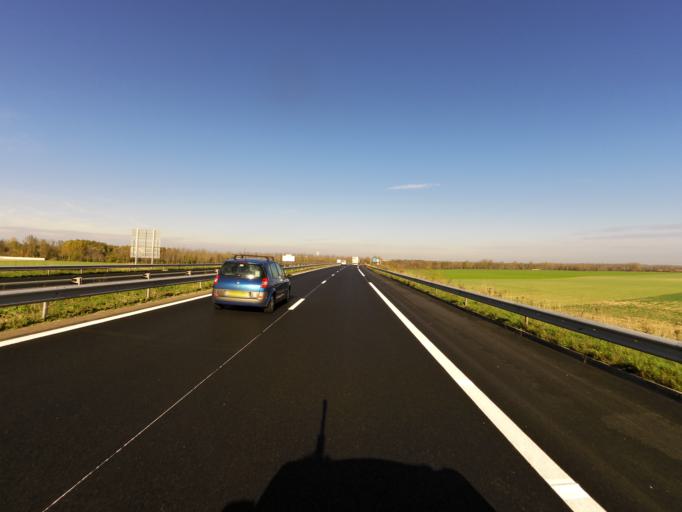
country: FR
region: Champagne-Ardenne
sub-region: Departement de la Marne
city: Fagnieres
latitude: 48.9619
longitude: 4.2860
